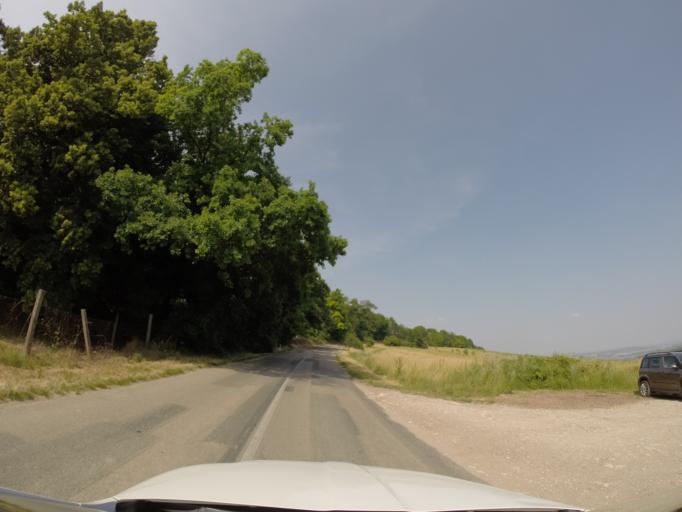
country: CZ
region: South Moravian
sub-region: Okres Breclav
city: Mikulov
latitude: 48.8549
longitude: 16.6442
